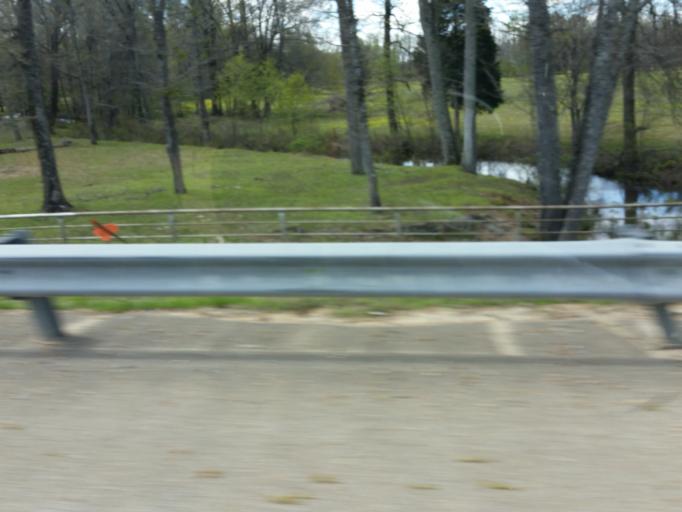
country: US
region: Arkansas
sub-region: Craighead County
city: Jonesboro
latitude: 35.9223
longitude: -90.7022
